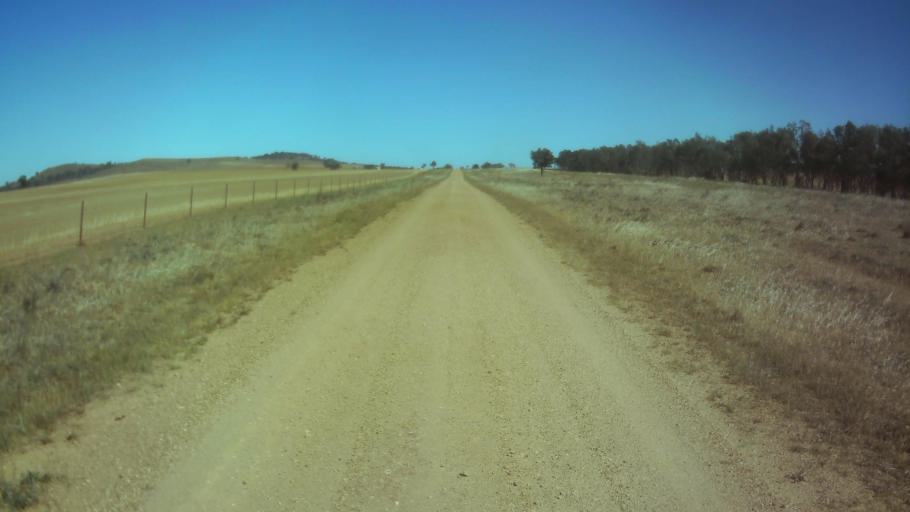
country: AU
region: New South Wales
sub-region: Weddin
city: Grenfell
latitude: -33.9690
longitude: 148.3152
